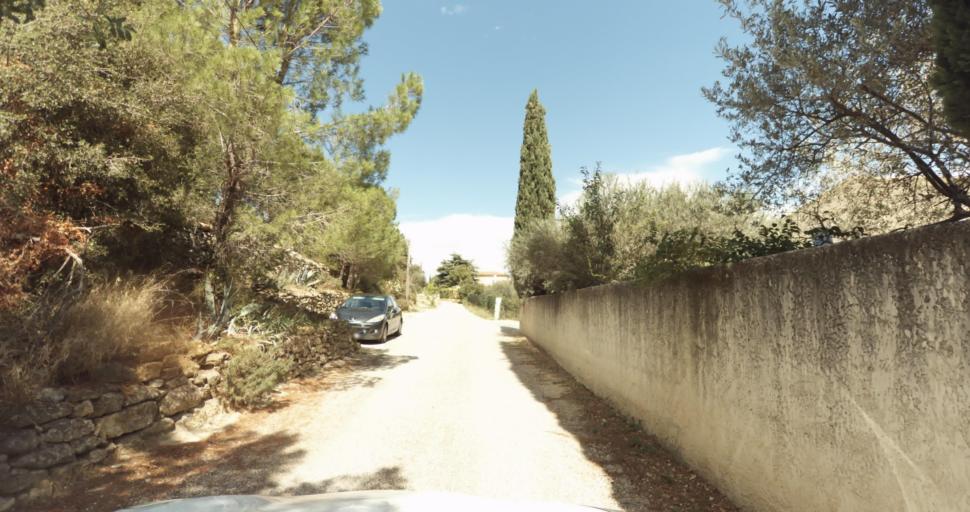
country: FR
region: Provence-Alpes-Cote d'Azur
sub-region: Departement des Bouches-du-Rhone
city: Miramas
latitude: 43.5814
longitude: 5.0201
